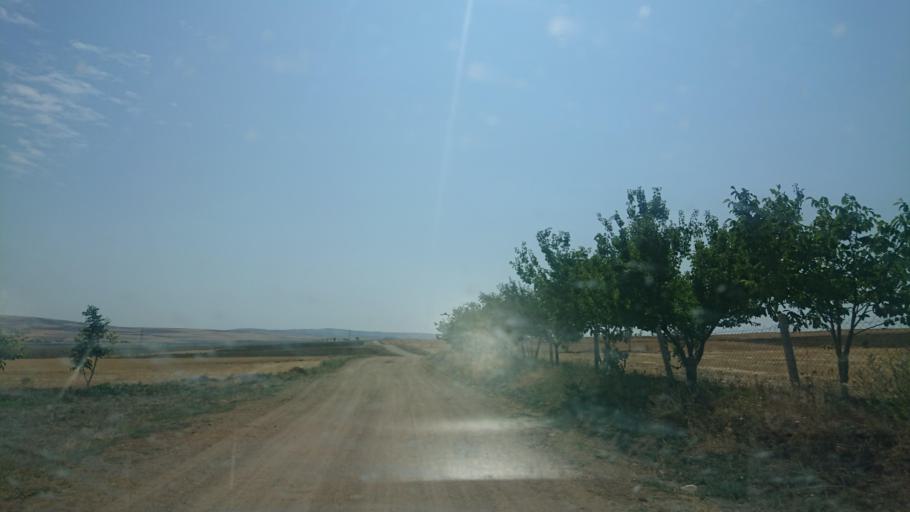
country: TR
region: Aksaray
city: Sariyahsi
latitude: 38.9572
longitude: 33.8999
